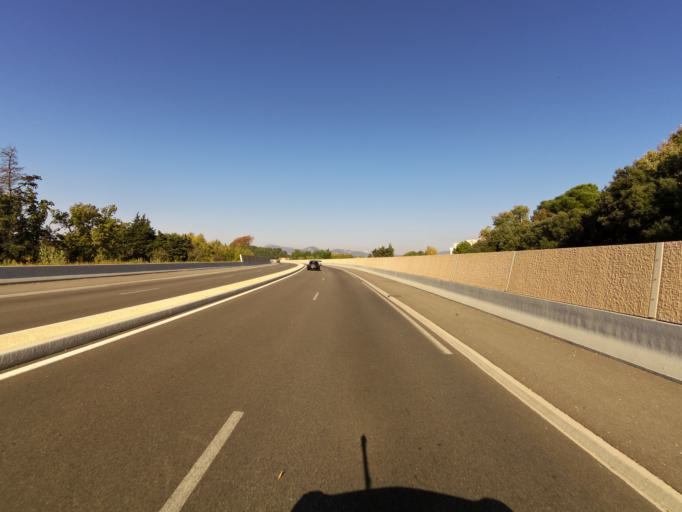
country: FR
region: Provence-Alpes-Cote d'Azur
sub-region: Departement du Vaucluse
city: Carpentras
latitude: 44.0500
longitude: 5.0289
